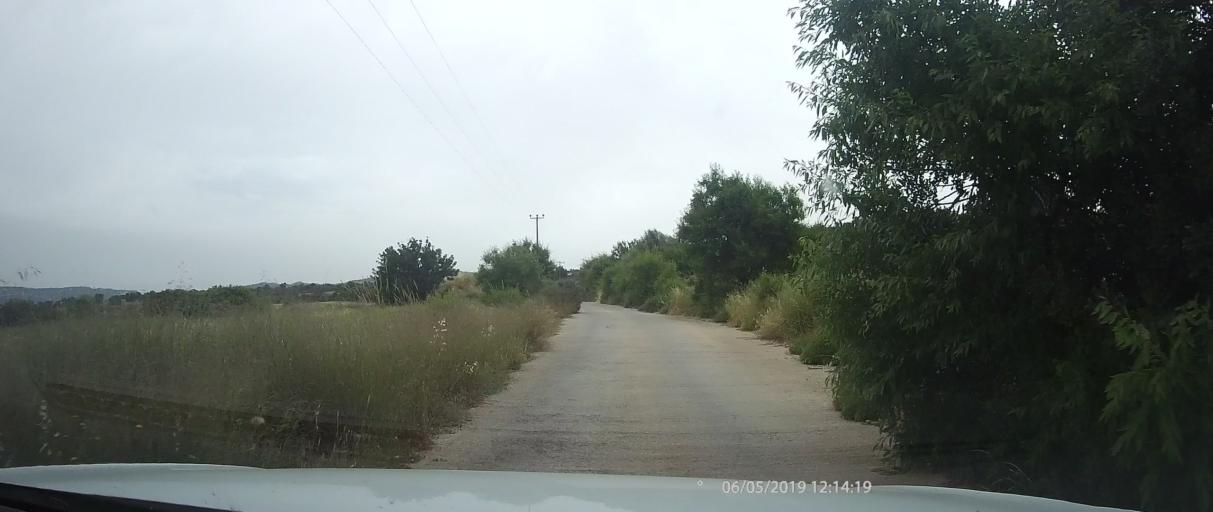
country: CY
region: Pafos
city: Tala
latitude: 34.8457
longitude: 32.4216
